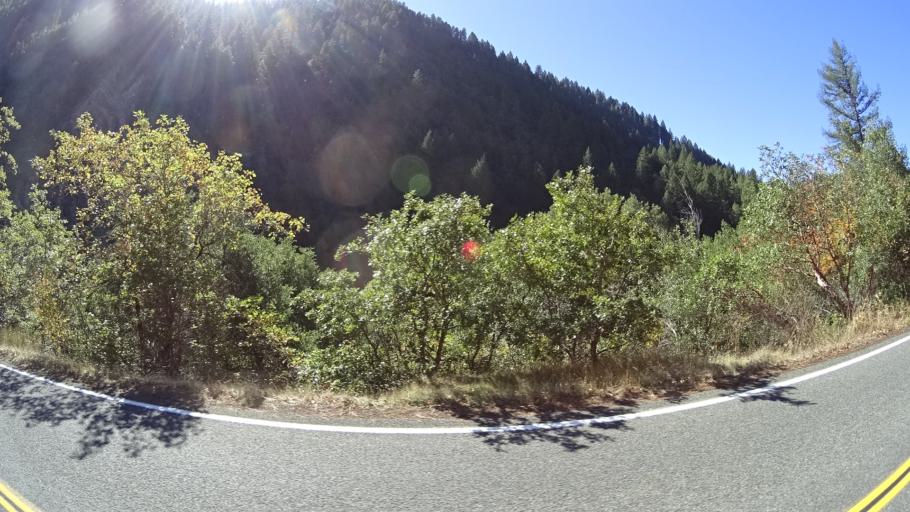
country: US
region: California
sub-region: Siskiyou County
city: Happy Camp
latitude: 41.3774
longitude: -123.4788
